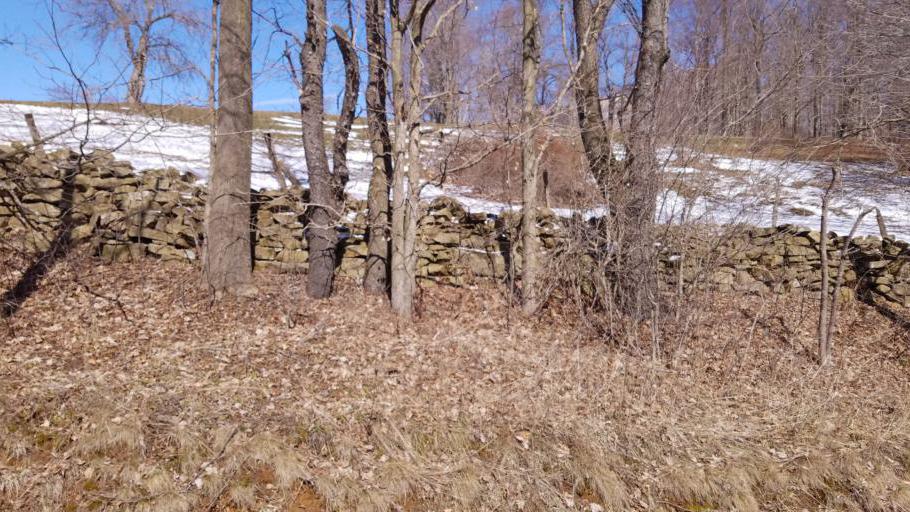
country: US
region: New York
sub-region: Allegany County
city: Andover
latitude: 41.9283
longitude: -77.7844
